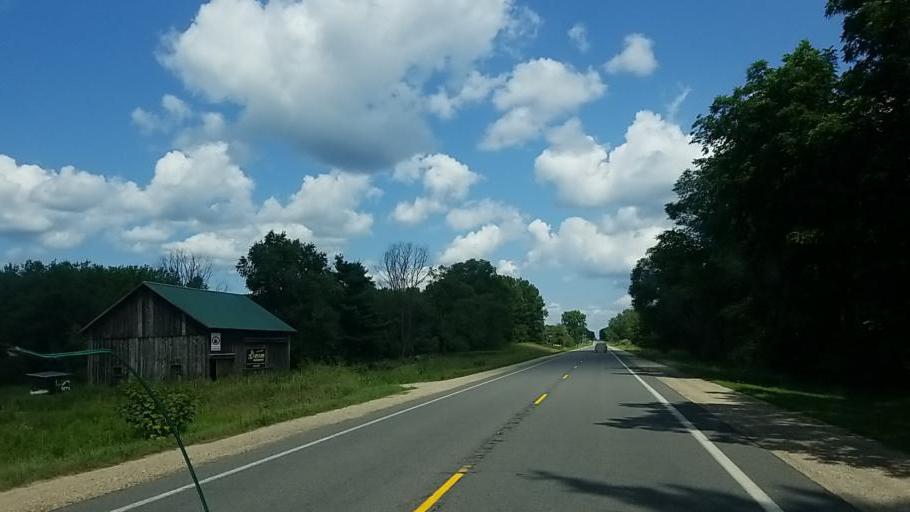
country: US
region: Michigan
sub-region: Montcalm County
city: Howard City
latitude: 43.3957
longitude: -85.6303
